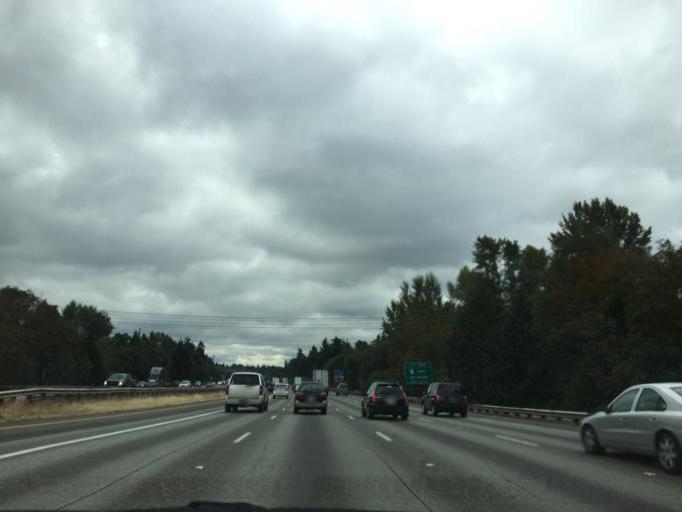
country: US
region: Washington
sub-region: King County
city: Des Moines
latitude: 47.4043
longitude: -122.2927
